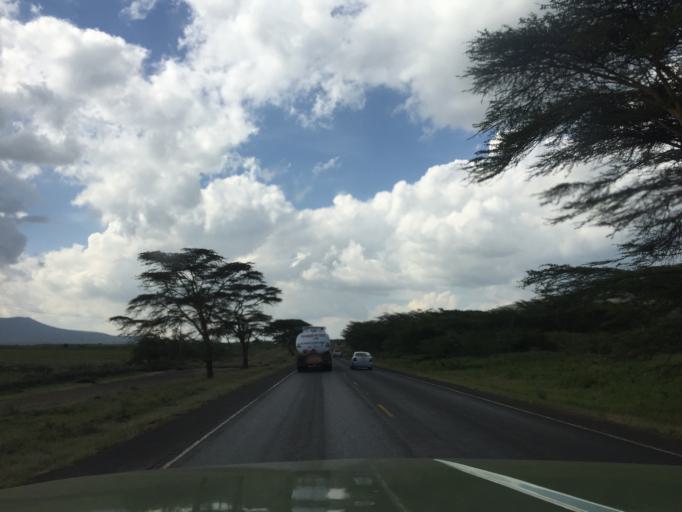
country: KE
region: Nakuru
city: Kijabe
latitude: -0.9469
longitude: 36.5471
